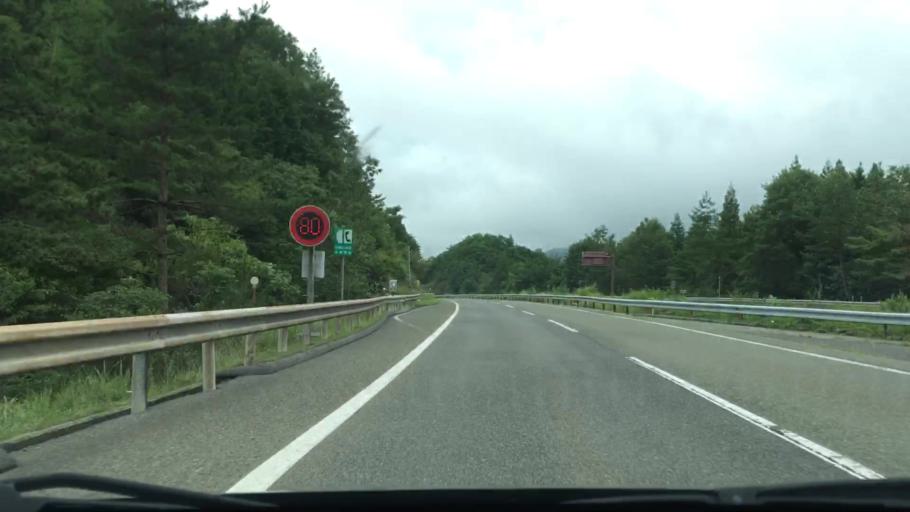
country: JP
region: Hiroshima
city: Shobara
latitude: 34.8750
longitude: 133.1216
